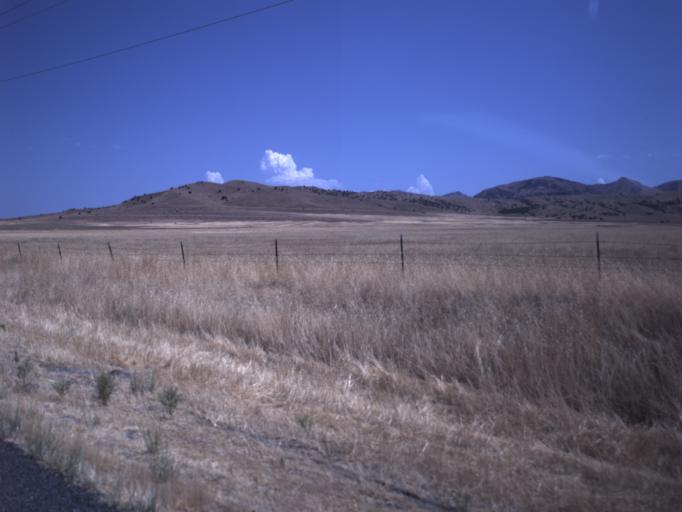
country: US
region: Utah
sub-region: Millard County
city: Delta
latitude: 39.4217
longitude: -112.3278
